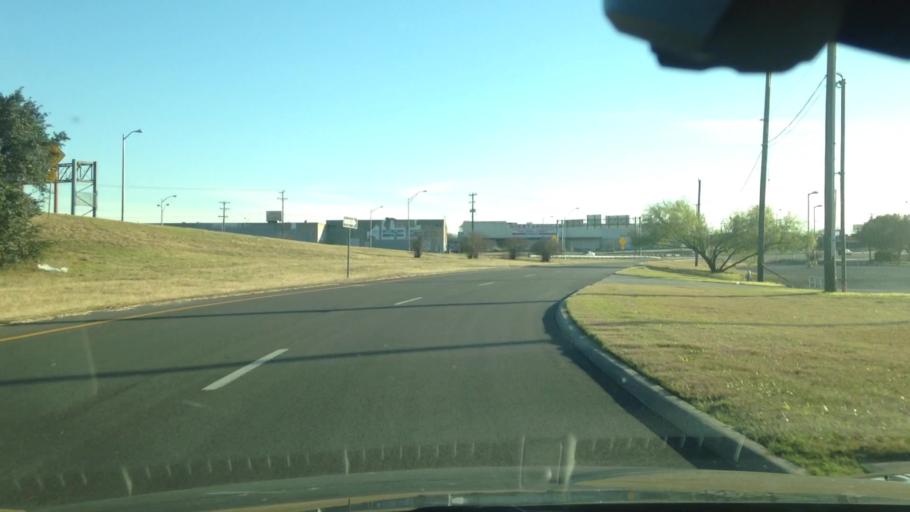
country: US
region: Texas
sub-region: Bexar County
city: Windcrest
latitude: 29.5148
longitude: -98.4039
